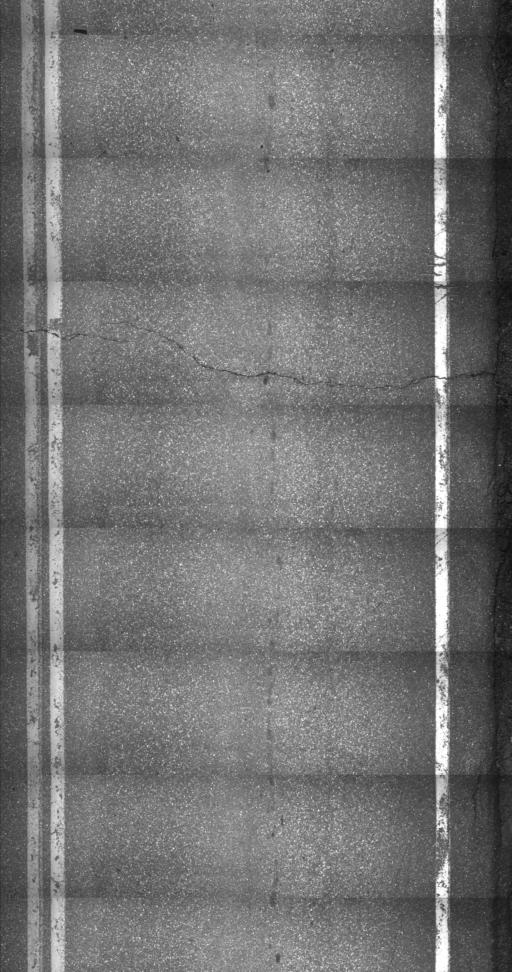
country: US
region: Vermont
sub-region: Orleans County
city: Newport
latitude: 44.9298
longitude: -72.0621
